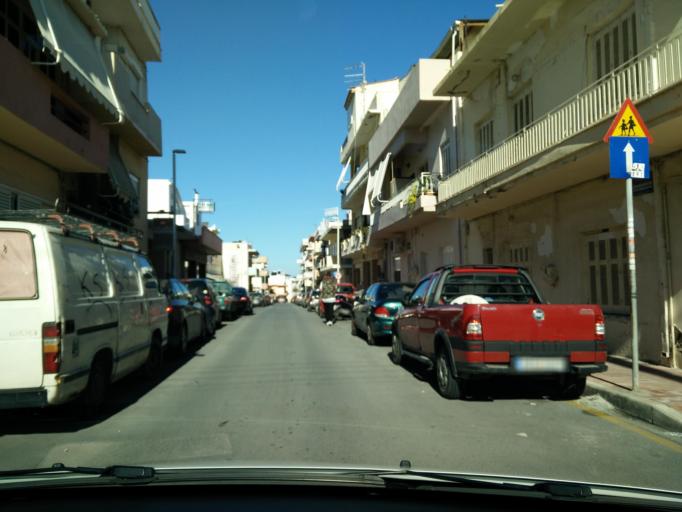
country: GR
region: Crete
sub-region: Nomos Irakleiou
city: Irakleion
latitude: 35.3329
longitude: 25.1448
